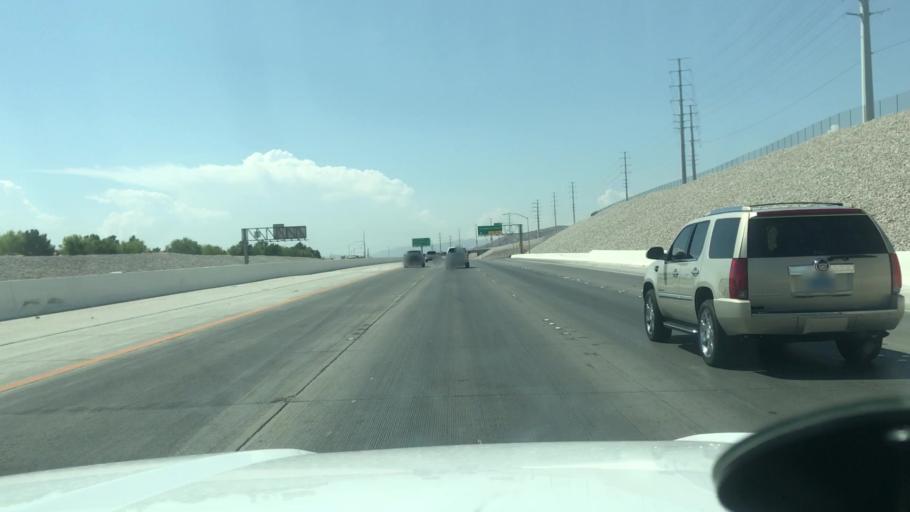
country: US
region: Nevada
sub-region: Clark County
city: Summerlin South
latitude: 36.1988
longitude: -115.3418
